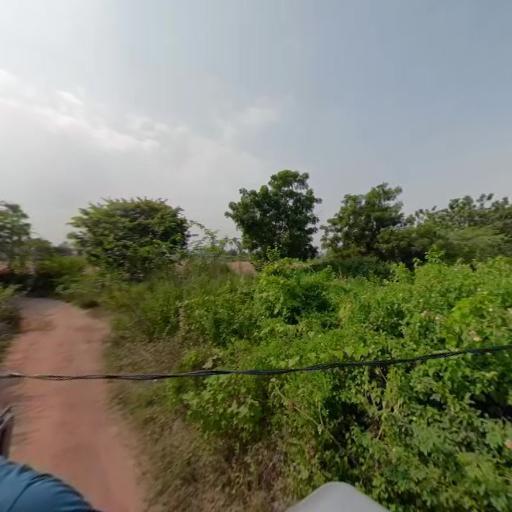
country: IN
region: Telangana
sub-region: Nalgonda
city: Suriapet
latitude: 17.2064
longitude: 79.4907
